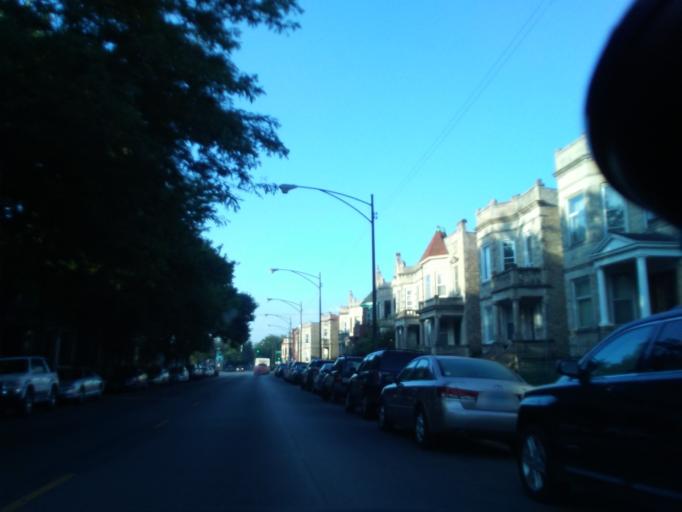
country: US
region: Illinois
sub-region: Cook County
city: Lincolnwood
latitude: 41.9261
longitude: -87.7122
